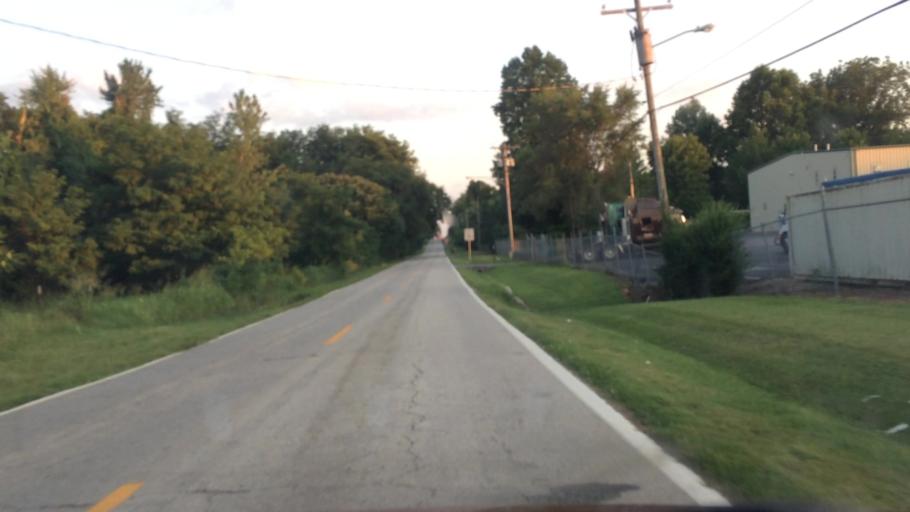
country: US
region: Missouri
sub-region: Greene County
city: Springfield
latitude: 37.2121
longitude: -93.3739
